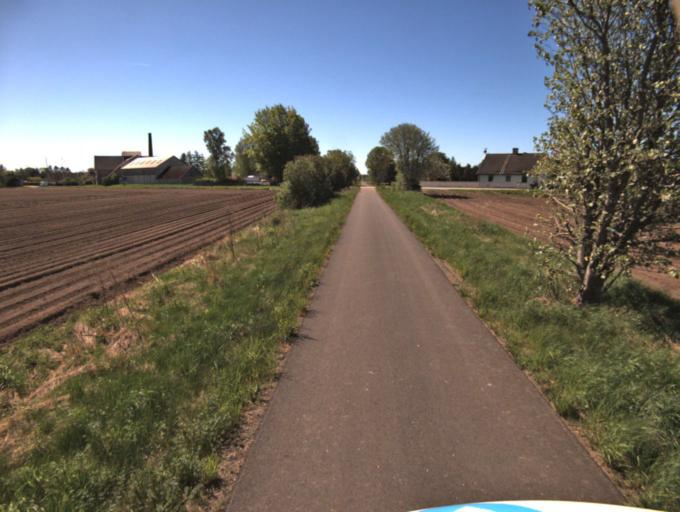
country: SE
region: Skane
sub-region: Kristianstads Kommun
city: Norra Asum
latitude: 55.9519
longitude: 14.1549
